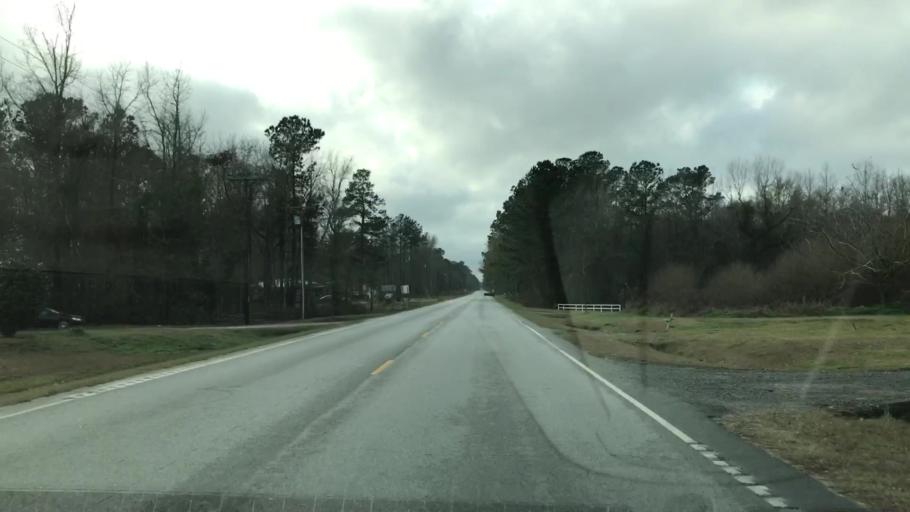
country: US
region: South Carolina
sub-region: Williamsburg County
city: Andrews
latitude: 33.2865
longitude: -79.7020
